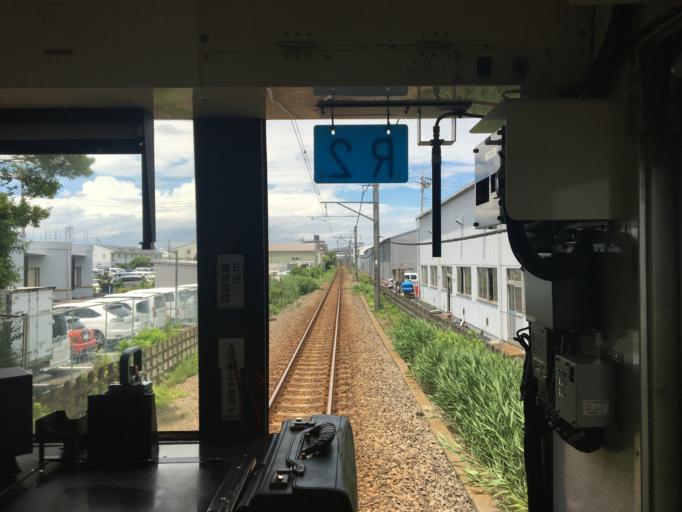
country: JP
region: Kanagawa
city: Atsugi
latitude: 35.4147
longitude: 139.3776
